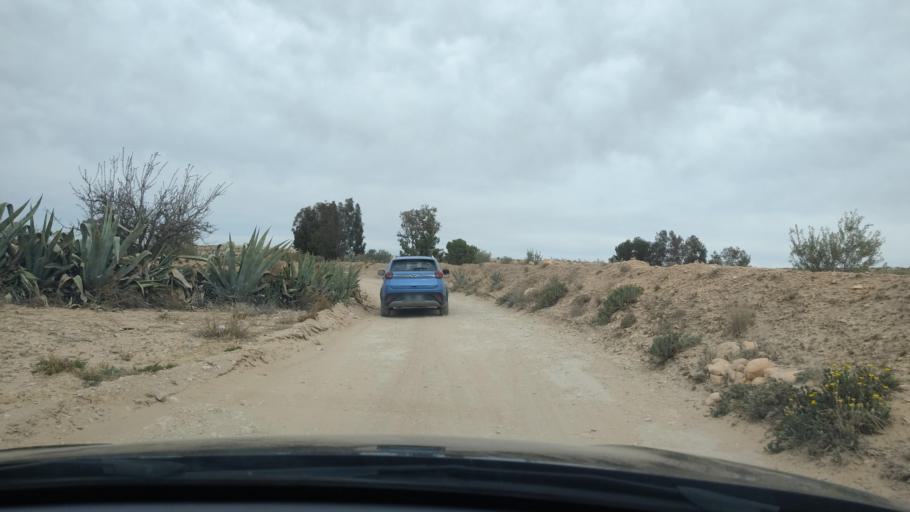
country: TN
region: Al Qasrayn
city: Kasserine
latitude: 35.2561
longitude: 8.9220
